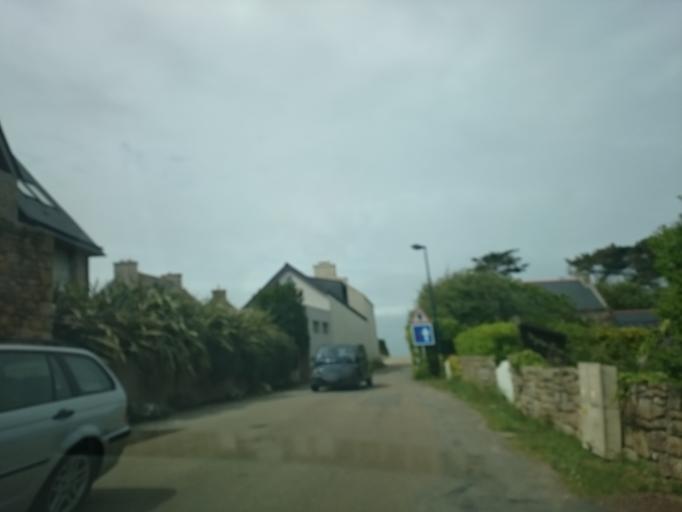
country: FR
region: Brittany
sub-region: Departement du Finistere
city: Landunvez
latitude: 48.5566
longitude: -4.7198
